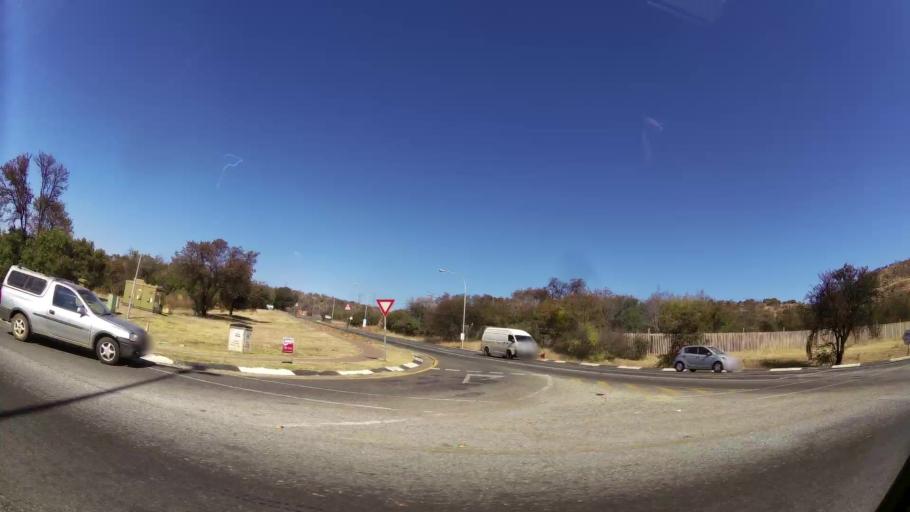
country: ZA
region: Gauteng
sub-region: City of Johannesburg Metropolitan Municipality
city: Johannesburg
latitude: -26.2872
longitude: 28.0359
